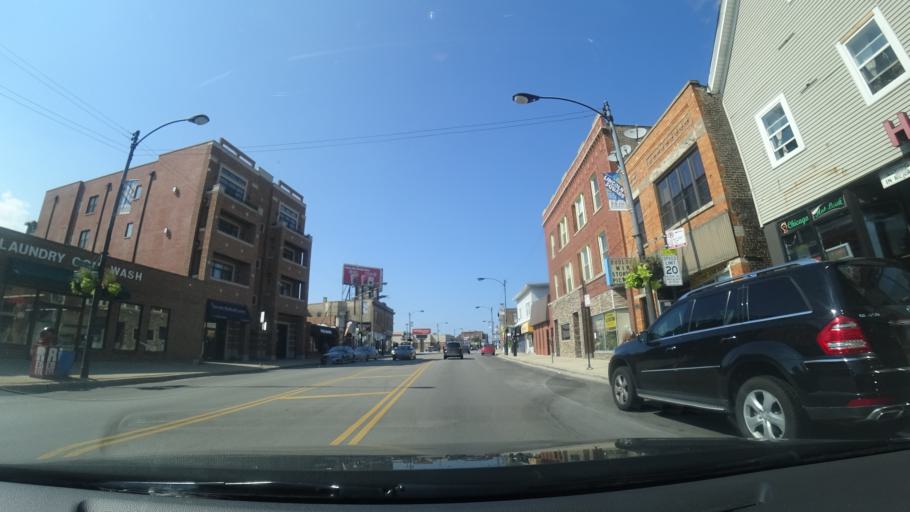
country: US
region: Illinois
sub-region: Cook County
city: Lincolnwood
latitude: 41.9740
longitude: -87.6920
